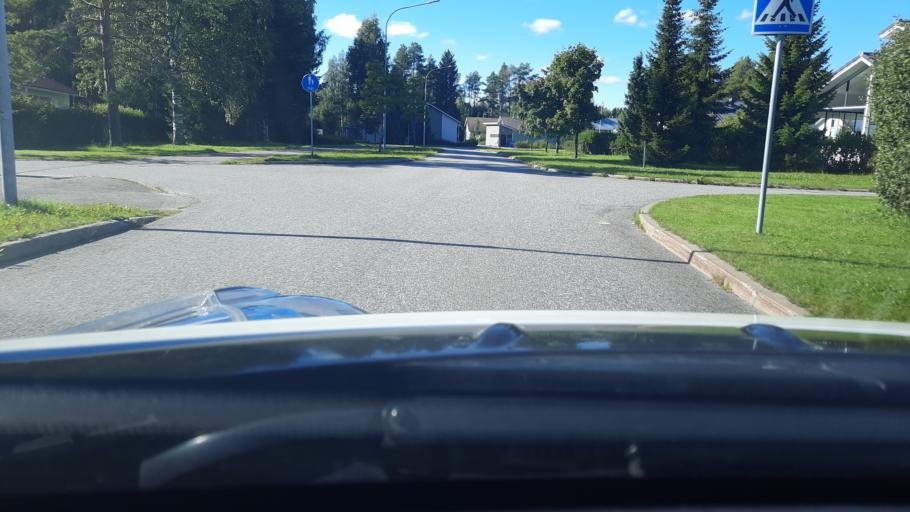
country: FI
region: North Karelia
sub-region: Joensuu
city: Joensuu
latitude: 62.6349
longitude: 29.6859
